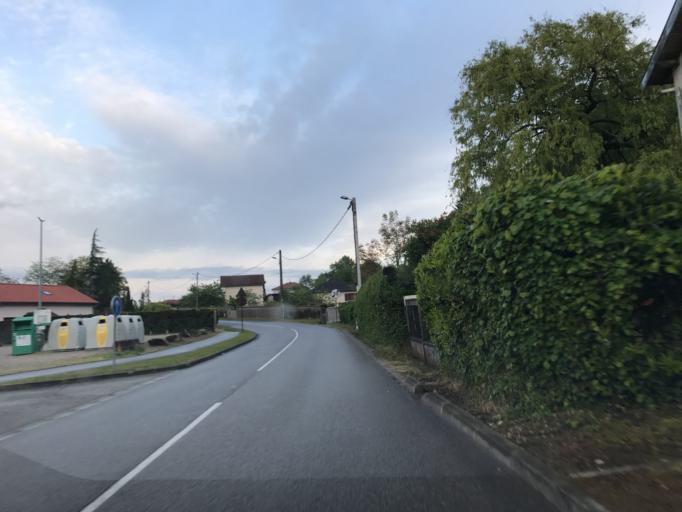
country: FR
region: Rhone-Alpes
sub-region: Departement de l'Ain
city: Montluel
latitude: 45.8583
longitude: 5.0511
